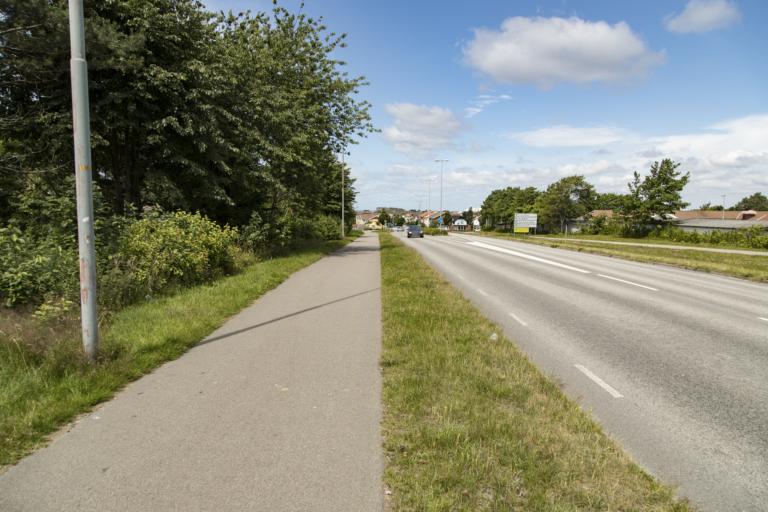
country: SE
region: Halland
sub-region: Varbergs Kommun
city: Varberg
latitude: 57.0934
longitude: 12.2592
